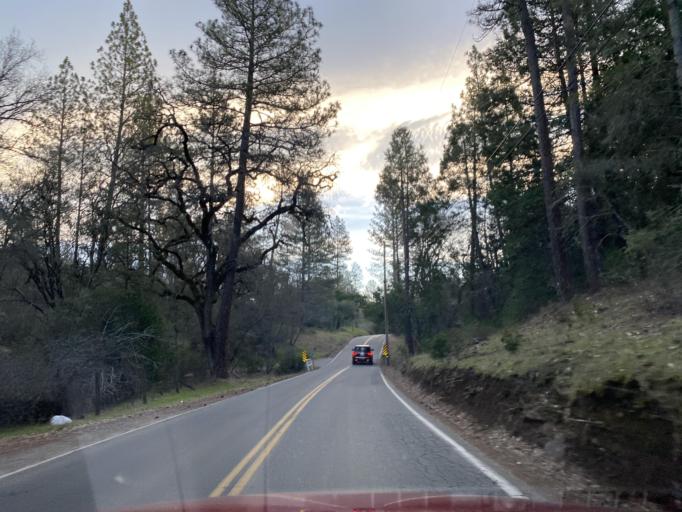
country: US
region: California
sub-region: Amador County
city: Pine Grove
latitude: 38.4972
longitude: -120.7215
